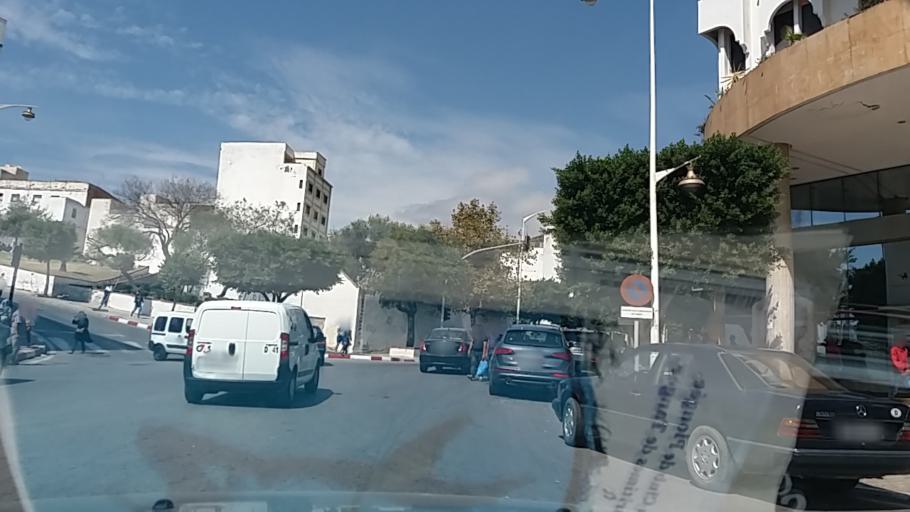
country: MA
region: Tanger-Tetouan
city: Tetouan
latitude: 35.5708
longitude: -5.3864
